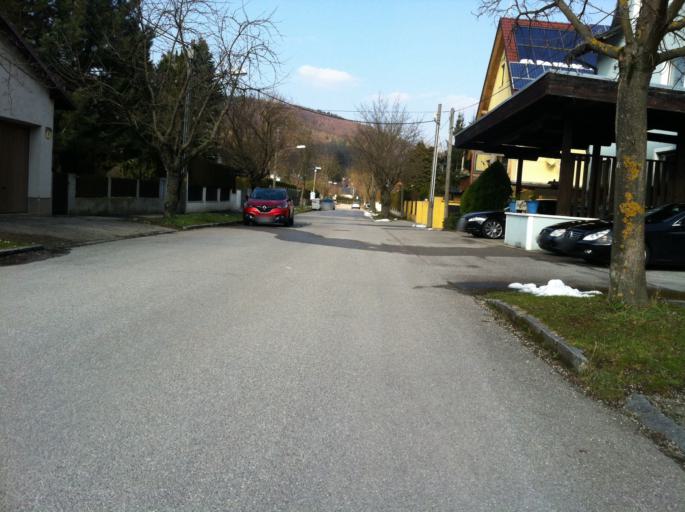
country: AT
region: Lower Austria
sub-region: Politischer Bezirk Wien-Umgebung
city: Wolfsgraben
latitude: 48.1878
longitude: 16.1272
